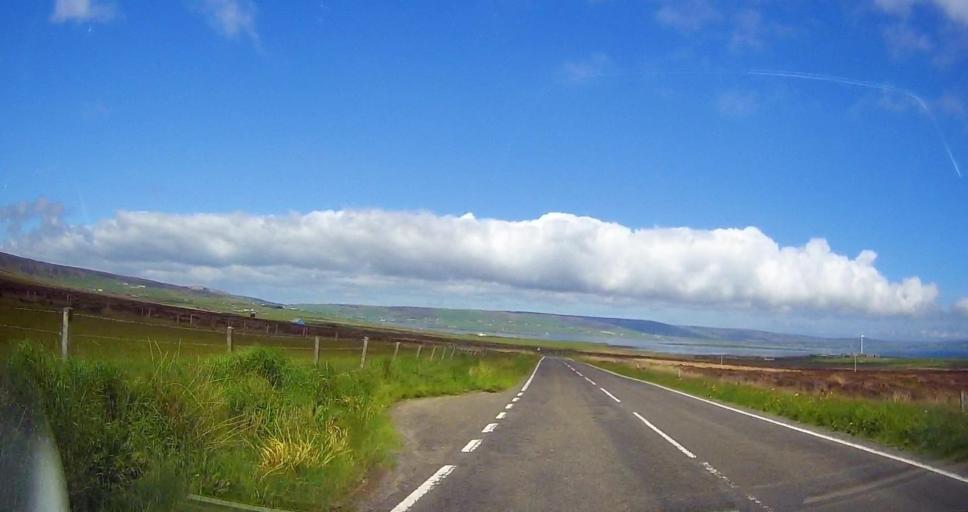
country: GB
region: Scotland
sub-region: Orkney Islands
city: Orkney
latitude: 58.9853
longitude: -3.0469
